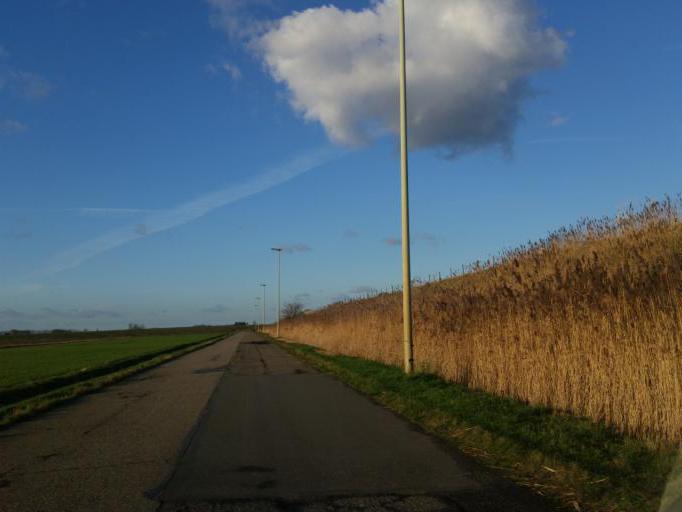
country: BE
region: Flanders
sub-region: Provincie Oost-Vlaanderen
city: Beveren
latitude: 51.3261
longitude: 4.2520
